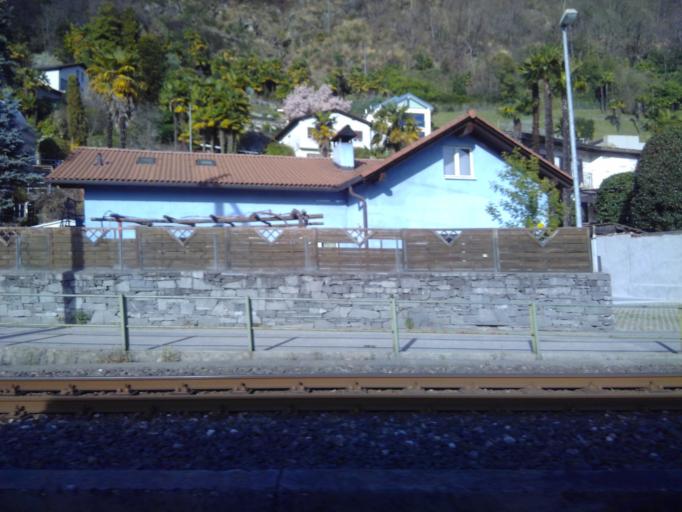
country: CH
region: Ticino
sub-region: Locarno District
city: Losone
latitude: 46.1730
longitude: 8.7690
